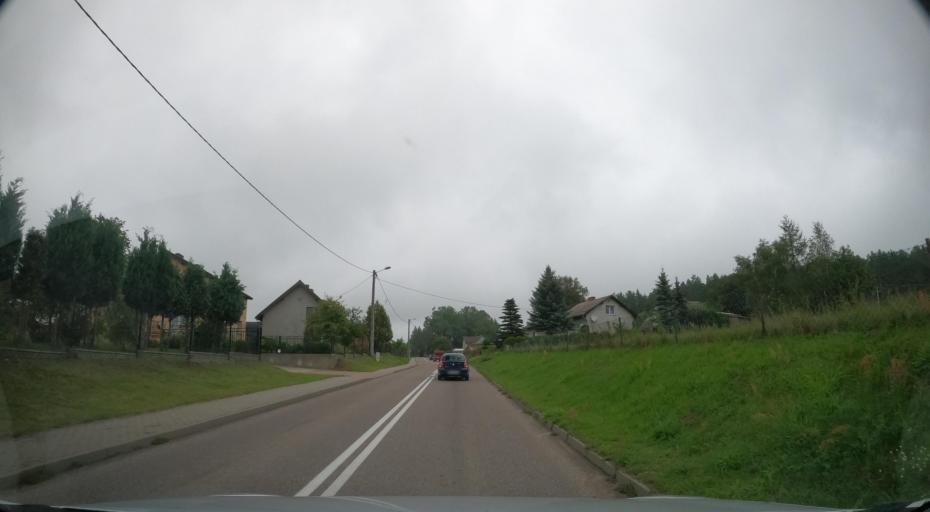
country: PL
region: Pomeranian Voivodeship
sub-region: Powiat wejherowski
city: Luzino
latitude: 54.4692
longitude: 18.0731
